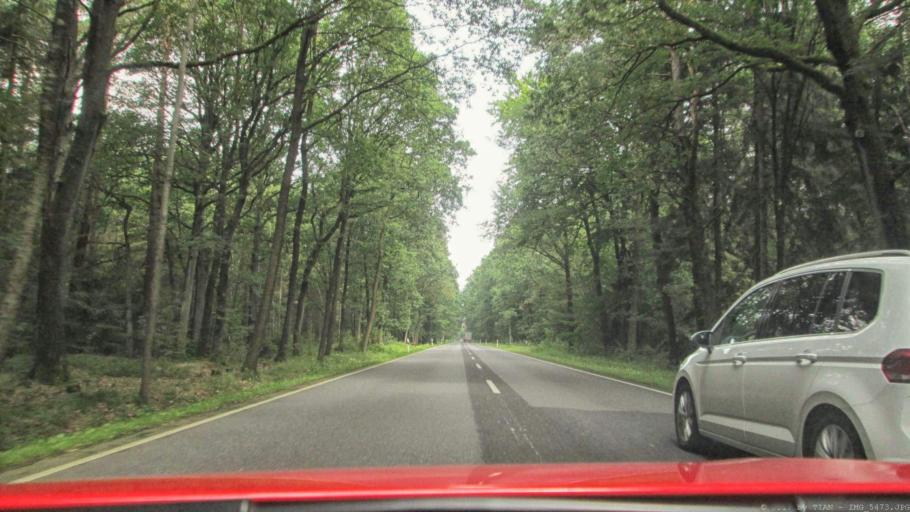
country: DE
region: Lower Saxony
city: Sprakensehl
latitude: 52.7460
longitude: 10.4892
